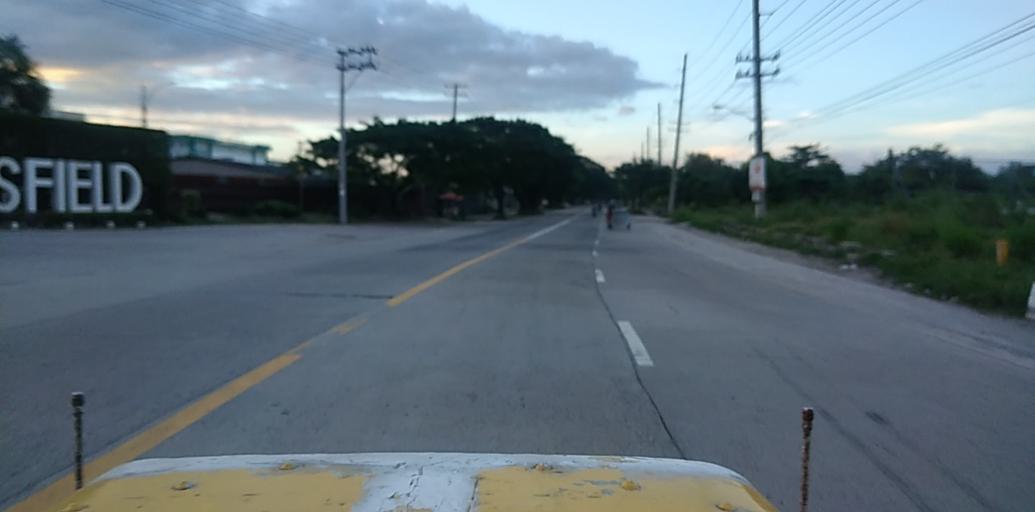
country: PH
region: Central Luzon
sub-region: Province of Pampanga
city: Calibutbut
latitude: 15.1187
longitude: 120.5905
